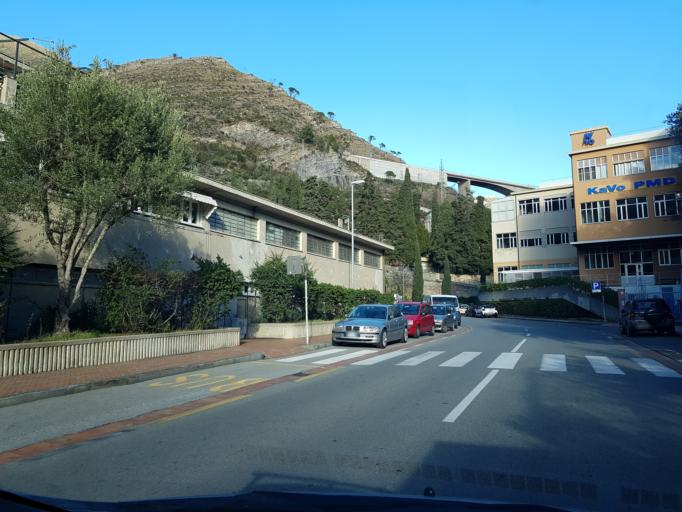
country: IT
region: Liguria
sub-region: Provincia di Genova
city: Bogliasco
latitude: 44.3889
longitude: 9.0356
